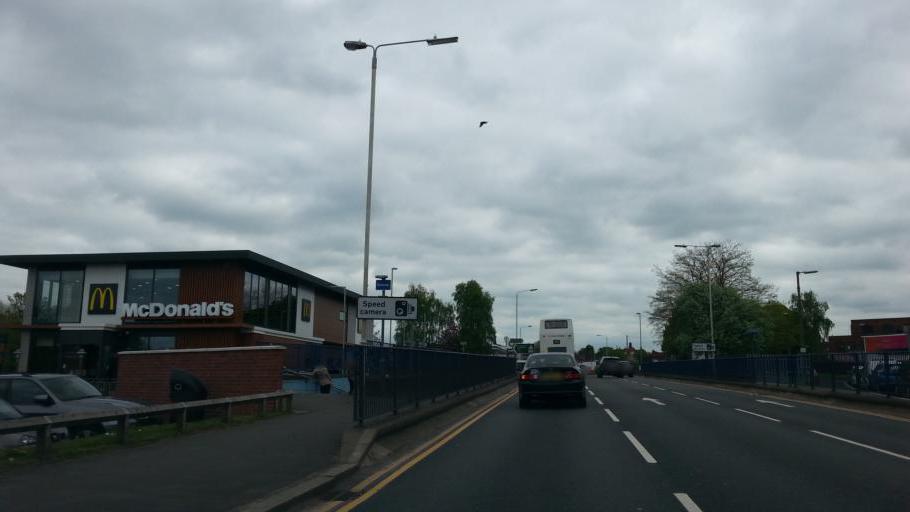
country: GB
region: England
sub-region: Dudley
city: Stourbridge
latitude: 52.4587
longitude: -2.1463
